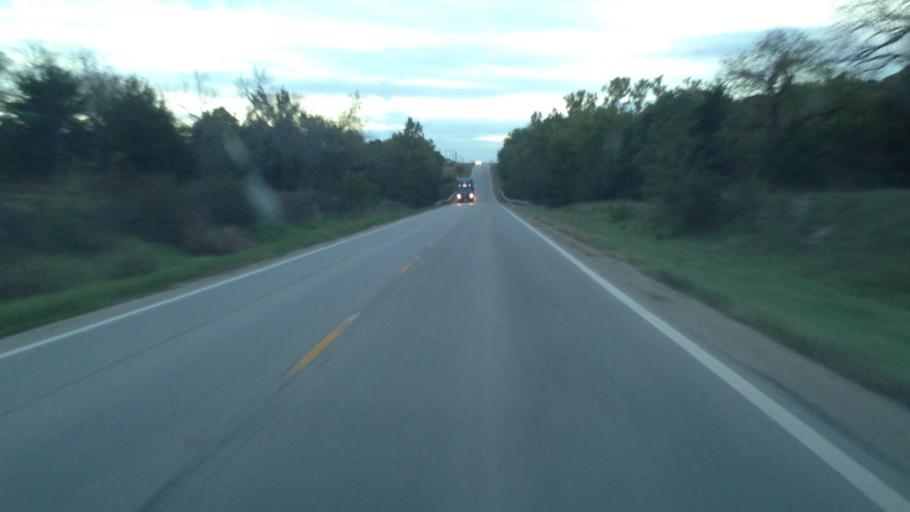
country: US
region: Kansas
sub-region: Anderson County
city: Garnett
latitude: 38.2349
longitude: -95.2481
